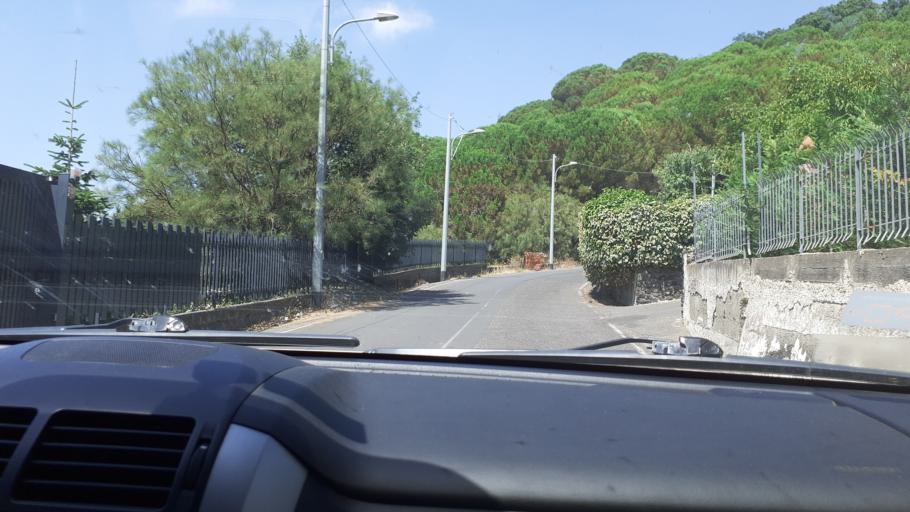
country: IT
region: Sicily
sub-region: Catania
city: Nicolosi
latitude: 37.6339
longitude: 15.0246
